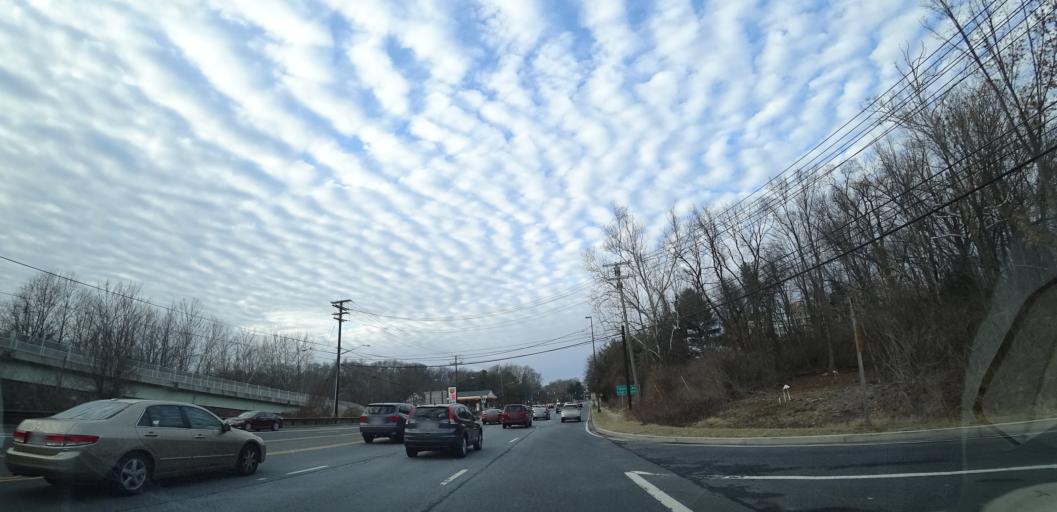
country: US
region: Maryland
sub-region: Montgomery County
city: Rockville
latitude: 39.0875
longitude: -77.1764
